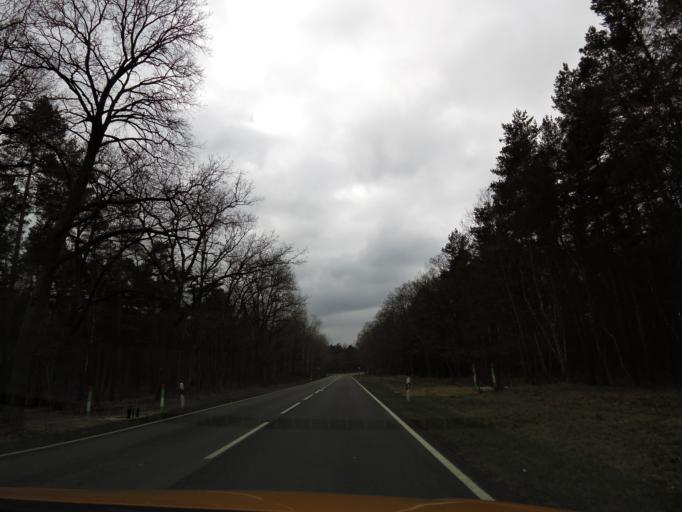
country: DE
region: Brandenburg
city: Nennhausen
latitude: 52.6103
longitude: 12.4207
